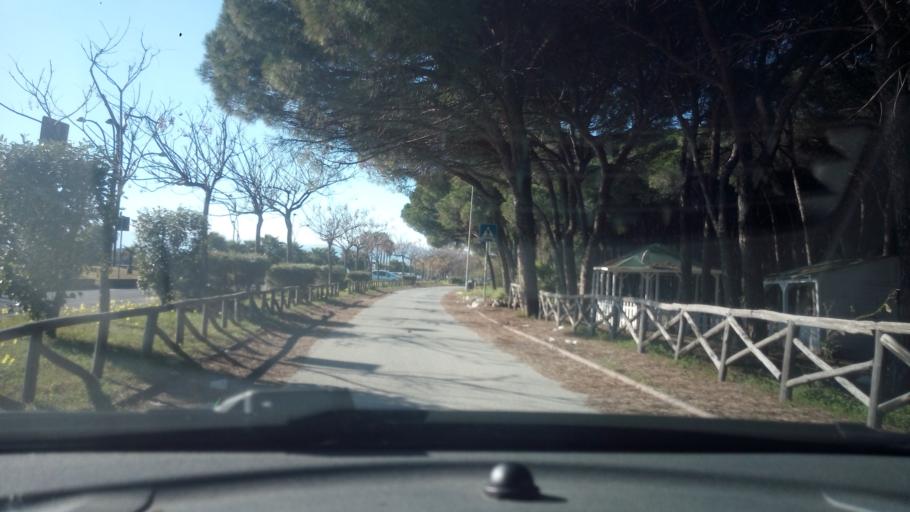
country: IT
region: Calabria
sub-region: Provincia di Catanzaro
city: Barone
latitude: 38.8318
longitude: 16.6452
